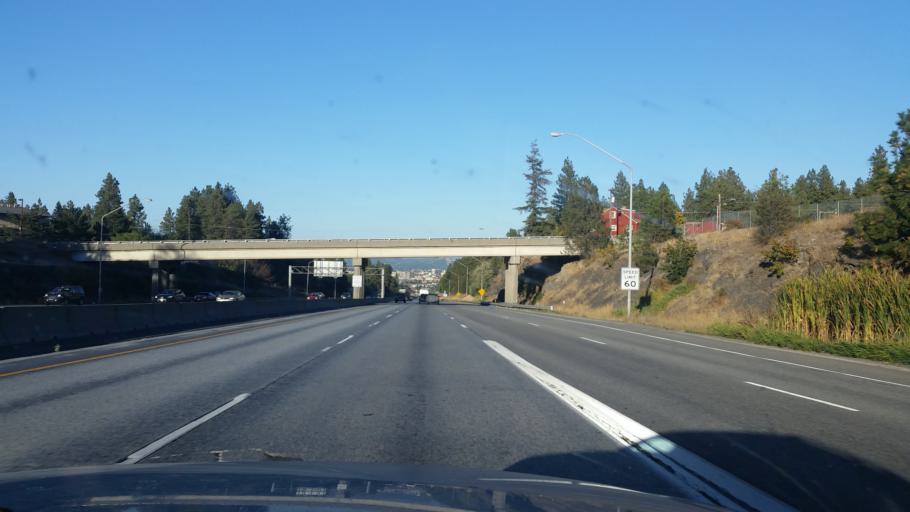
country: US
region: Washington
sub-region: Spokane County
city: Spokane
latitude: 47.6369
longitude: -117.4734
